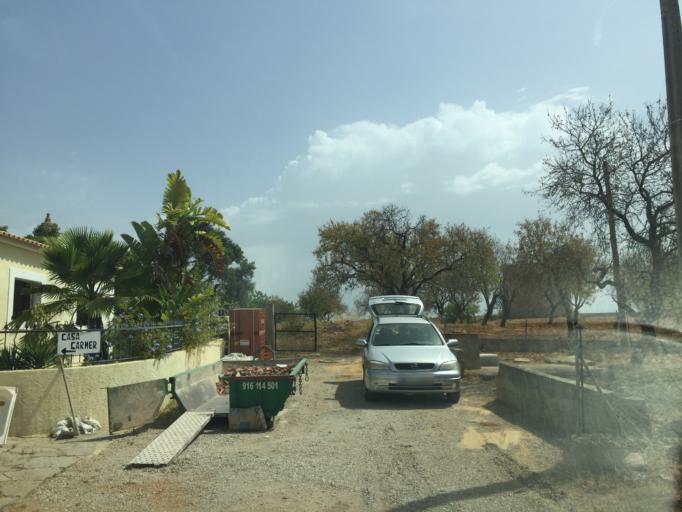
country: PT
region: Faro
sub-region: Loule
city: Boliqueime
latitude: 37.1299
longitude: -8.1403
